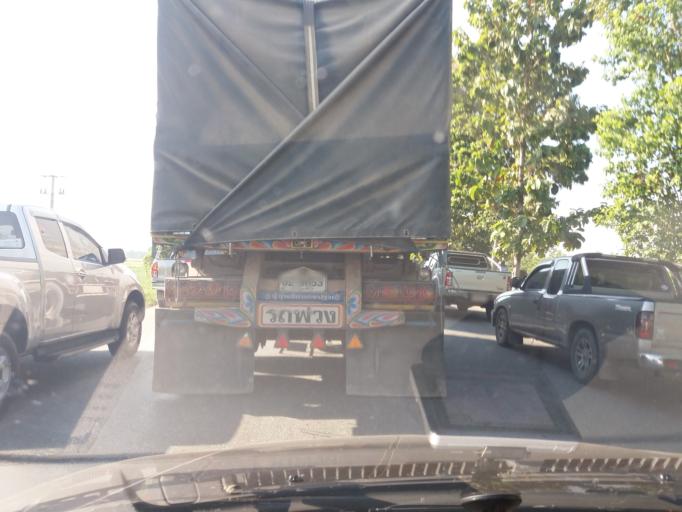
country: TH
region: Nakhon Sawan
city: Nakhon Sawan
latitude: 15.7356
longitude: 100.0244
